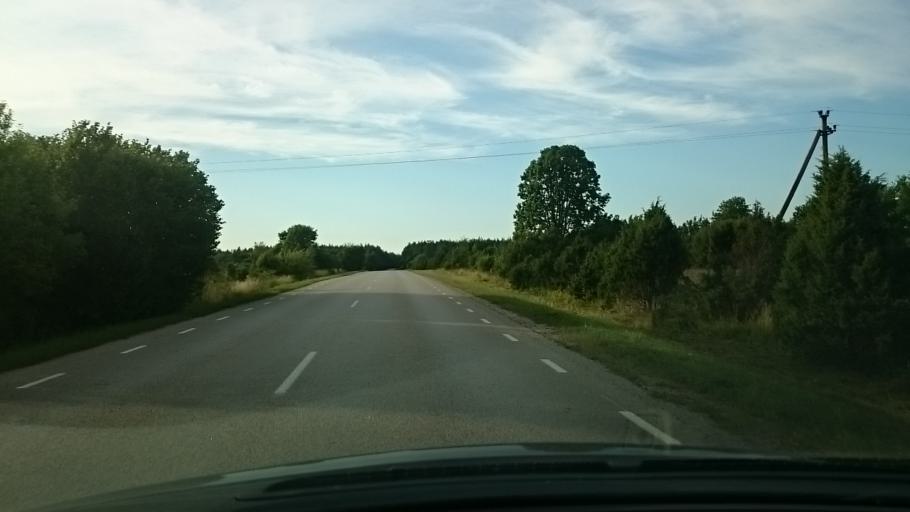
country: EE
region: Saare
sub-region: Kuressaare linn
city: Kuressaare
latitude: 58.3410
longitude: 22.3748
